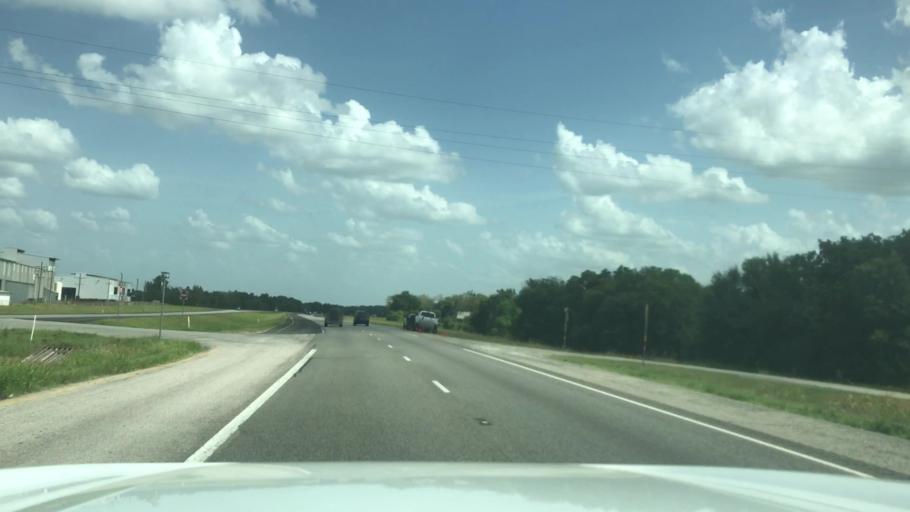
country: US
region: Texas
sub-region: Grimes County
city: Navasota
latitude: 30.3562
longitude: -96.0597
